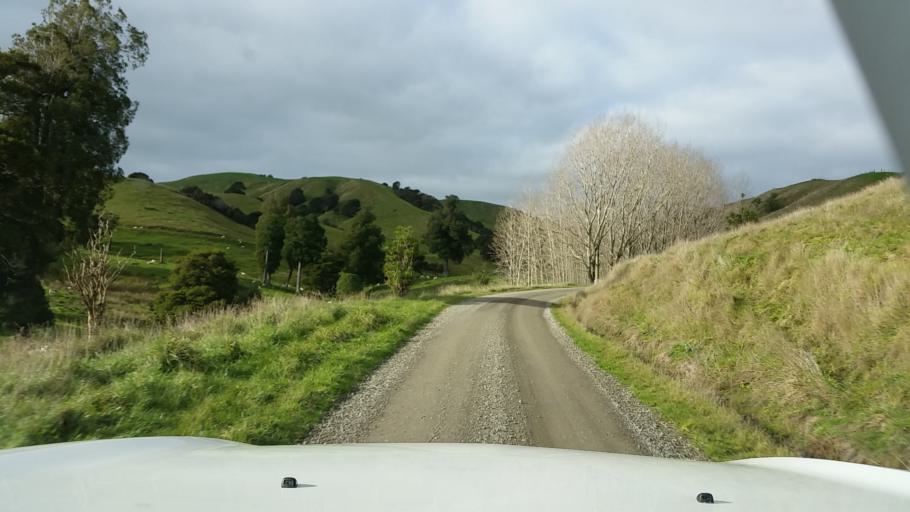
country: NZ
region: Wellington
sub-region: Masterton District
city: Masterton
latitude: -41.0416
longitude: 175.7266
